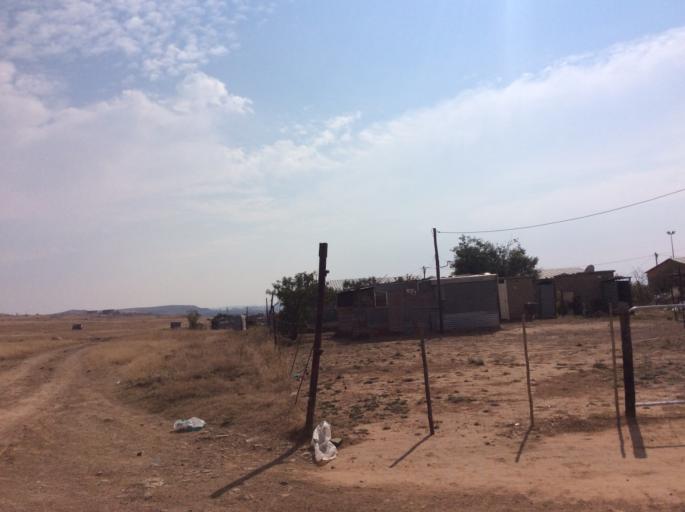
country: ZA
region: Orange Free State
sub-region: Xhariep District Municipality
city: Dewetsdorp
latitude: -29.5972
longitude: 26.6785
